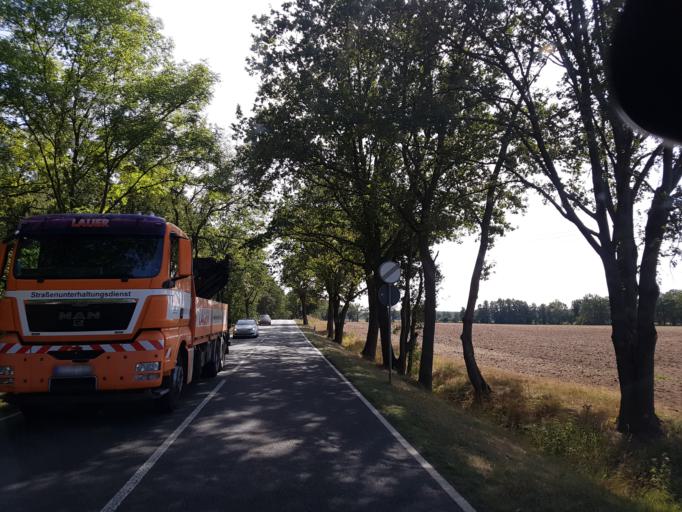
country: DE
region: Brandenburg
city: Luckau
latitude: 51.7888
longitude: 13.6886
